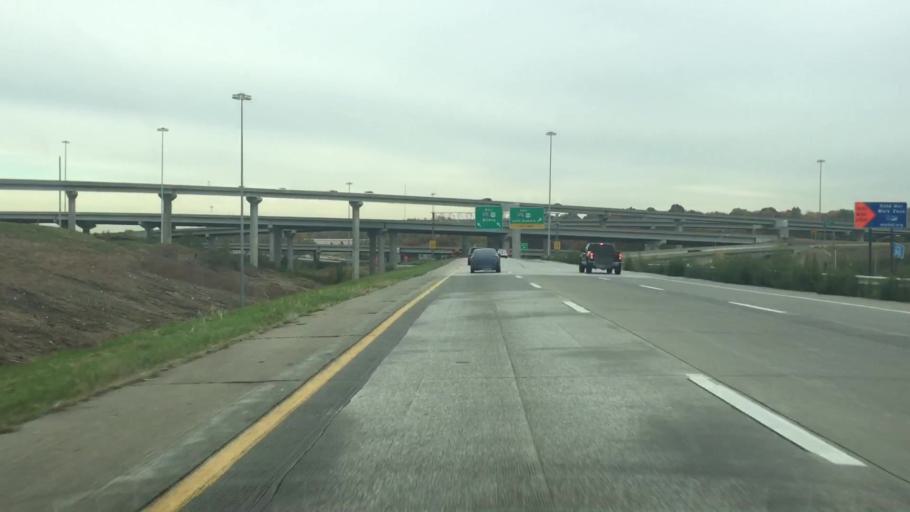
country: US
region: Missouri
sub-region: Jackson County
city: Grandview
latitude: 38.9296
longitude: -94.5266
